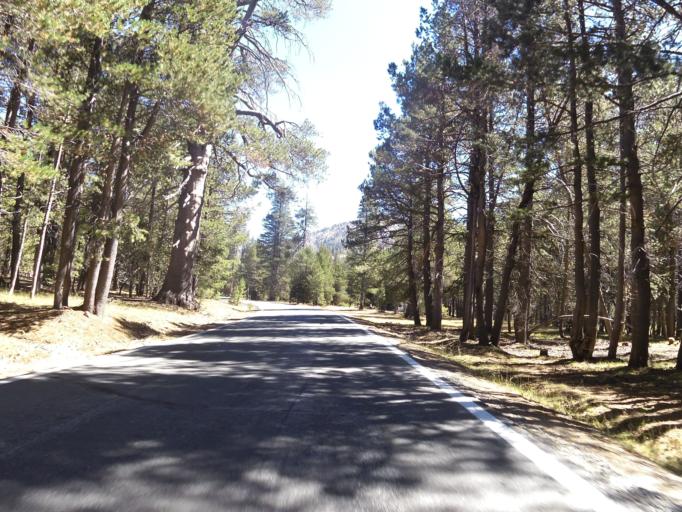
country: US
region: Nevada
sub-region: Douglas County
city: Gardnerville Ranchos
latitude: 38.5385
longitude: -119.8939
